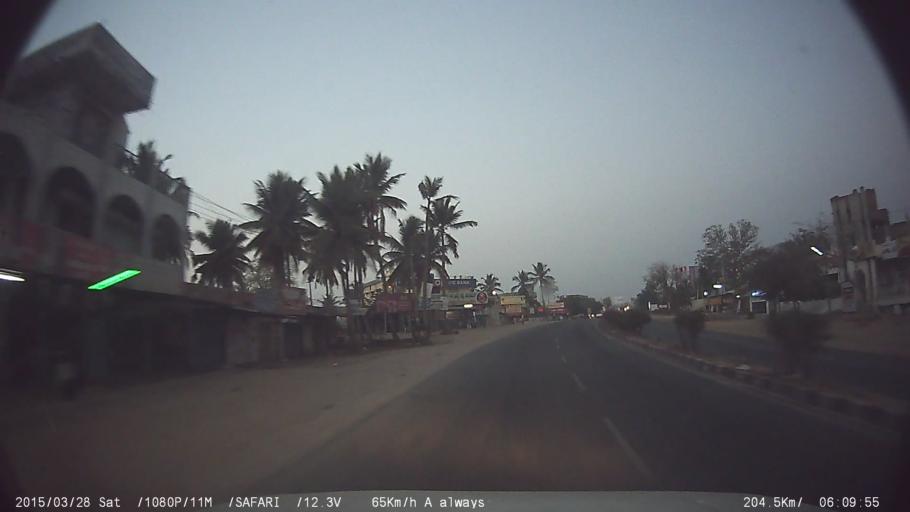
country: IN
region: Karnataka
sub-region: Ramanagara
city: Ramanagaram
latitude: 12.7946
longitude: 77.3821
